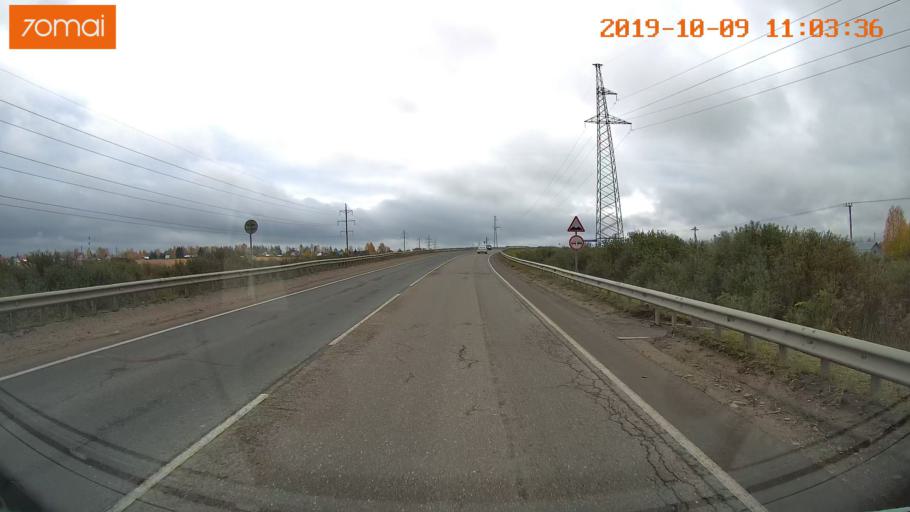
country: RU
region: Vologda
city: Vologda
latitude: 59.2194
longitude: 39.7737
